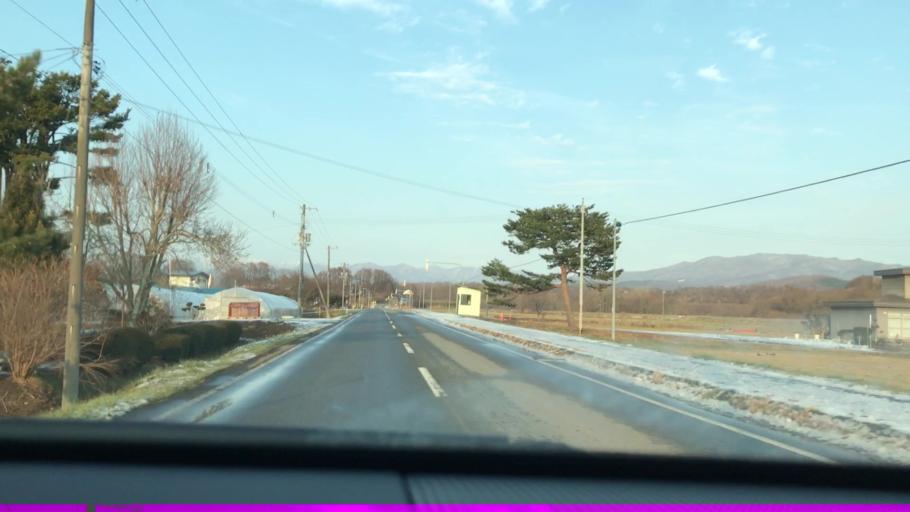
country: JP
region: Hokkaido
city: Shizunai-furukawacho
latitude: 42.4204
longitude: 142.3992
